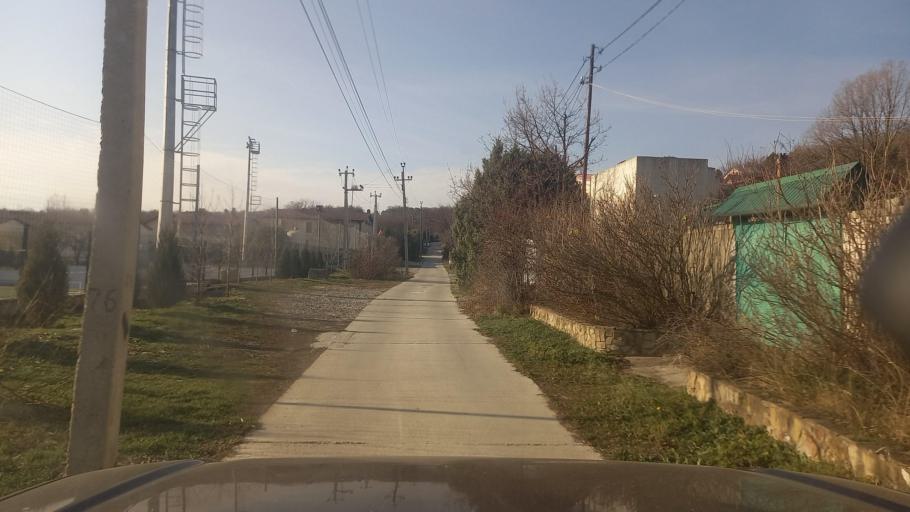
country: RU
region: Krasnodarskiy
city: Myskhako
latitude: 44.6663
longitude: 37.6797
